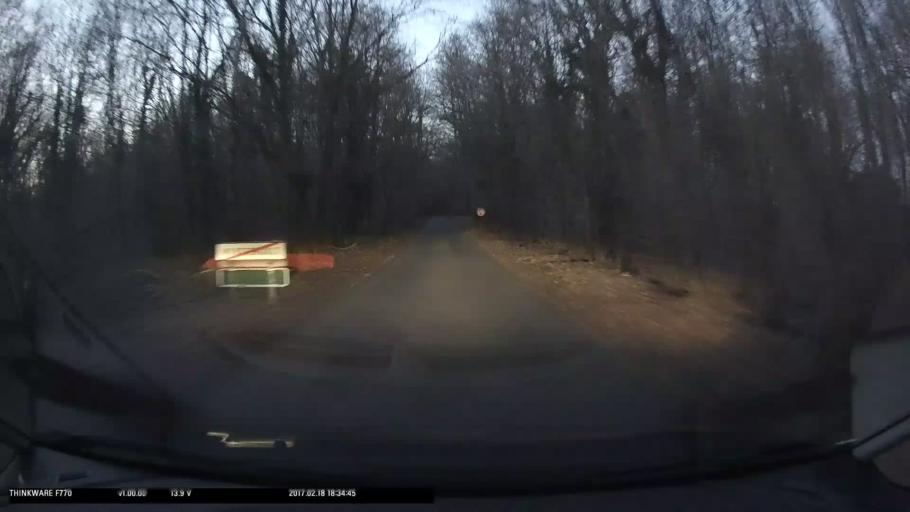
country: FR
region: Ile-de-France
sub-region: Departement du Val-d'Oise
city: Ableiges
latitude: 49.0877
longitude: 2.0030
